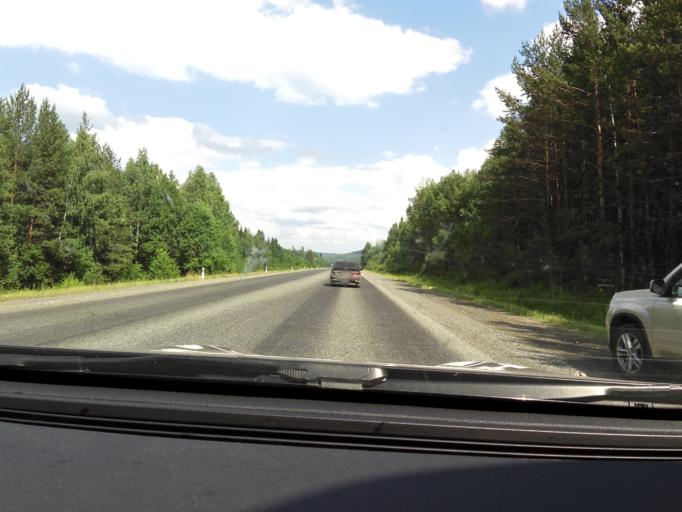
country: RU
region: Sverdlovsk
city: Arti
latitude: 56.7894
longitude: 58.5870
